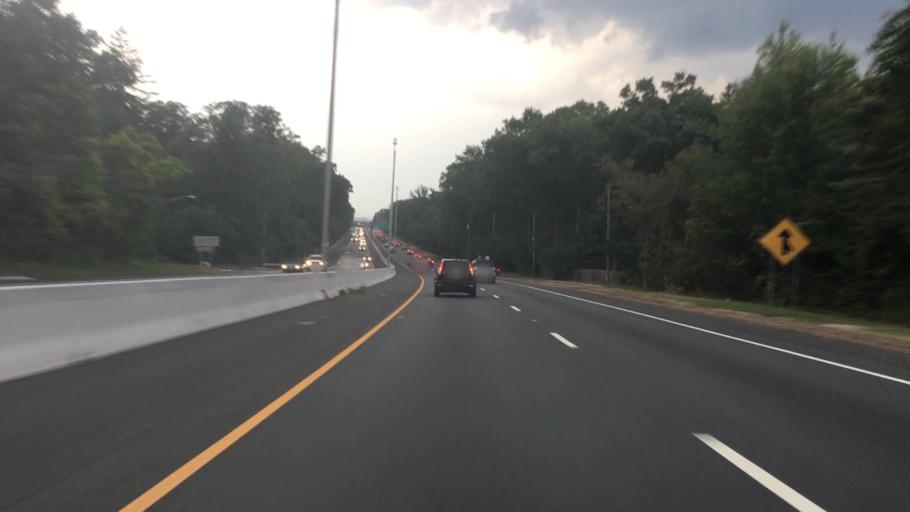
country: US
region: New Jersey
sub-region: Bergen County
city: Franklin Lakes
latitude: 41.0075
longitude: -74.1931
